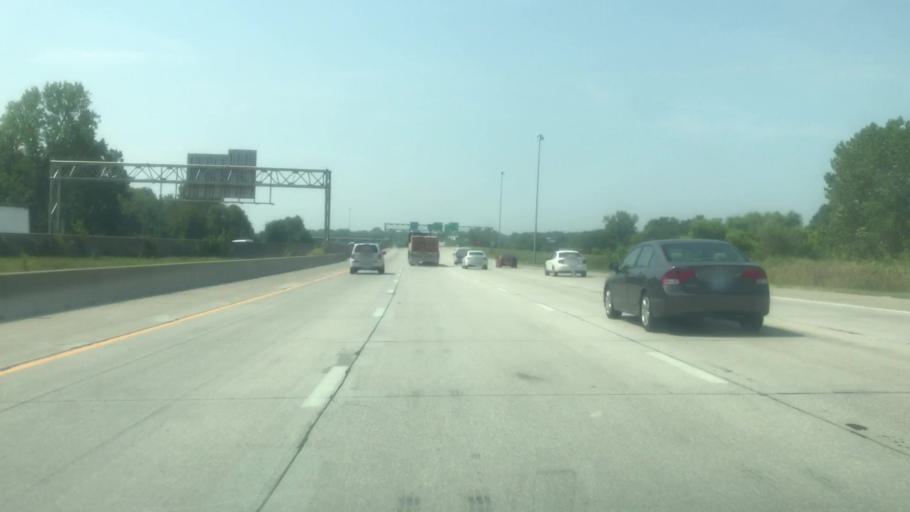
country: US
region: Kansas
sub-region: Johnson County
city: Merriam
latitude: 39.0385
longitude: -94.6806
